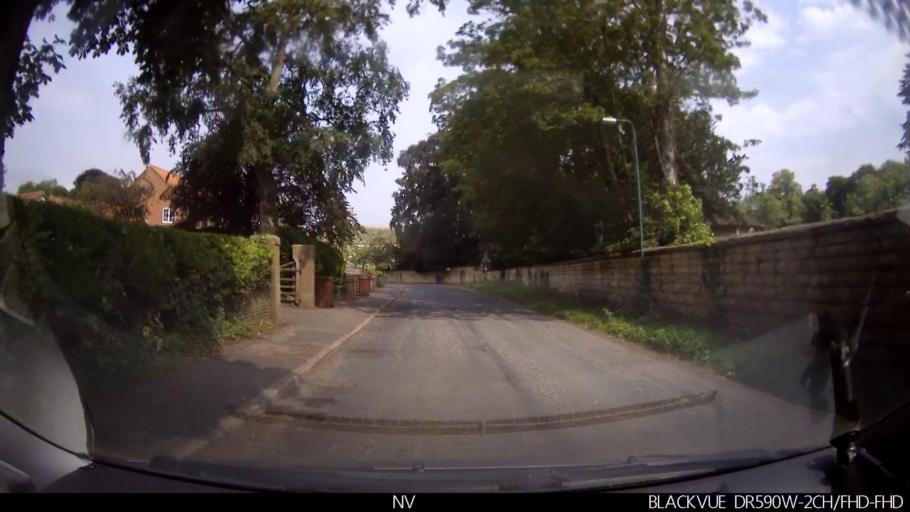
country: GB
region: England
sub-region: North Yorkshire
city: Great Habton
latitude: 54.2050
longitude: -0.8068
